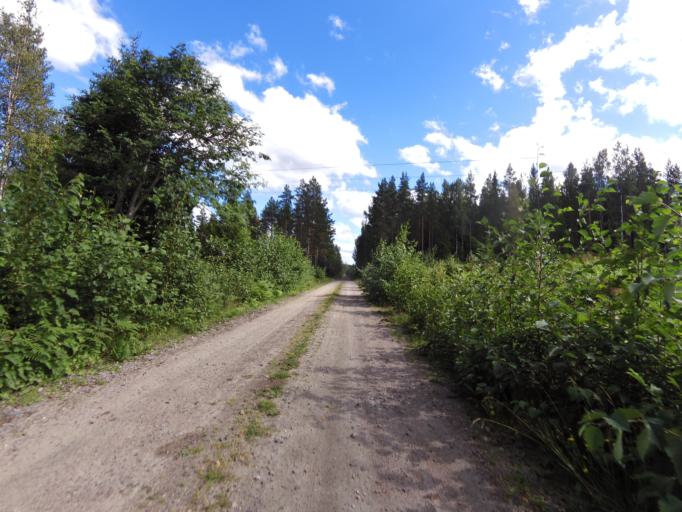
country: SE
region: Gaevleborg
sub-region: Hofors Kommun
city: Hofors
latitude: 60.5215
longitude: 16.2522
